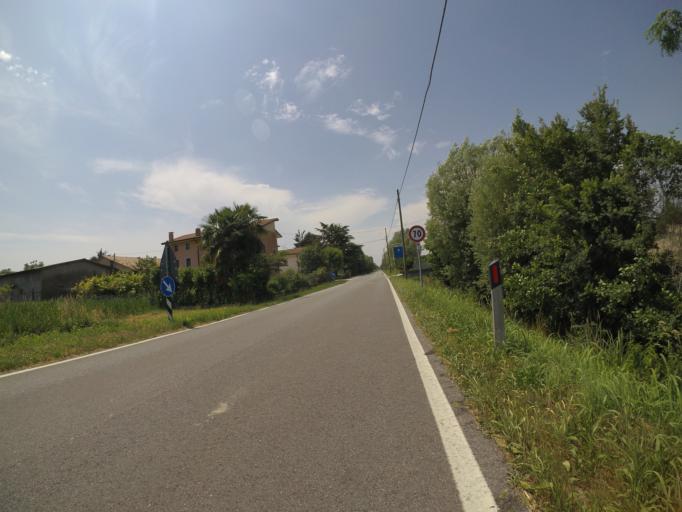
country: IT
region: Friuli Venezia Giulia
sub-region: Provincia di Udine
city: Teor
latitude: 45.8712
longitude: 13.0682
